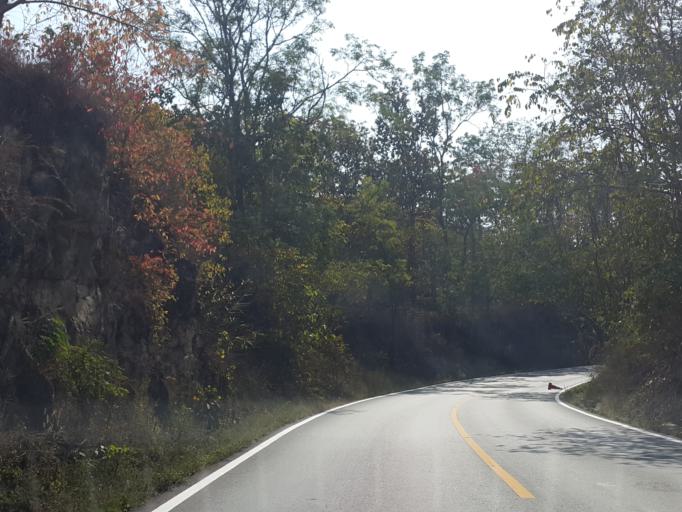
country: TH
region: Chiang Mai
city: Hot
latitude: 18.1811
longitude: 98.4524
